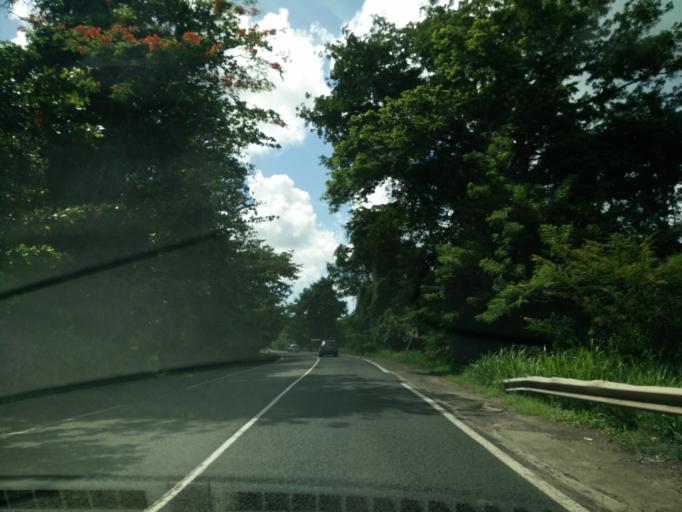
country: MQ
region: Martinique
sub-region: Martinique
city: Les Trois-Ilets
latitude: 14.5312
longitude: -61.0221
